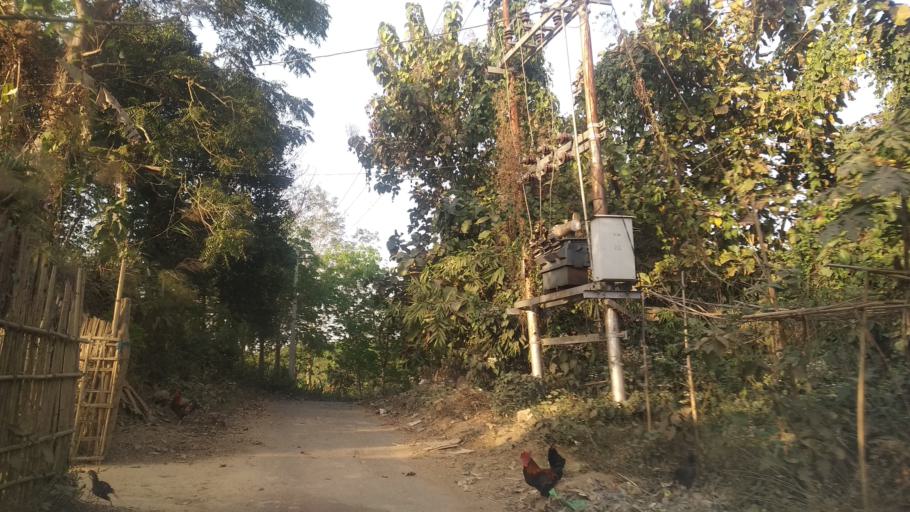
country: IN
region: Tripura
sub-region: West Tripura
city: Sonamura
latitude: 23.4440
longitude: 91.3720
